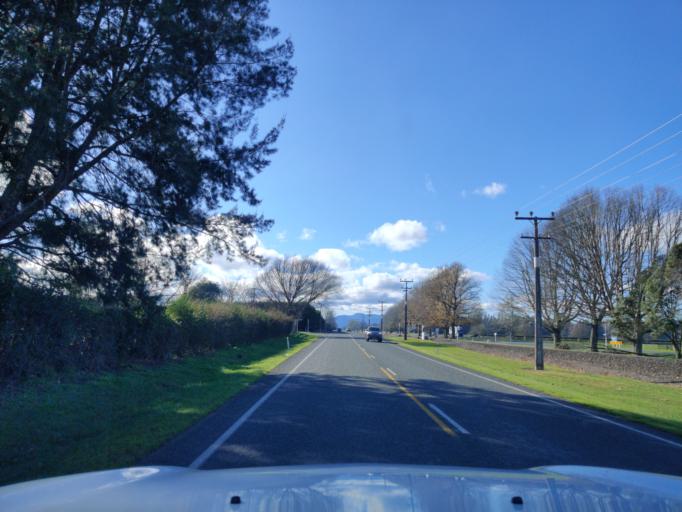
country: NZ
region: Waikato
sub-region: Matamata-Piako District
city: Matamata
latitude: -37.8538
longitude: 175.7578
